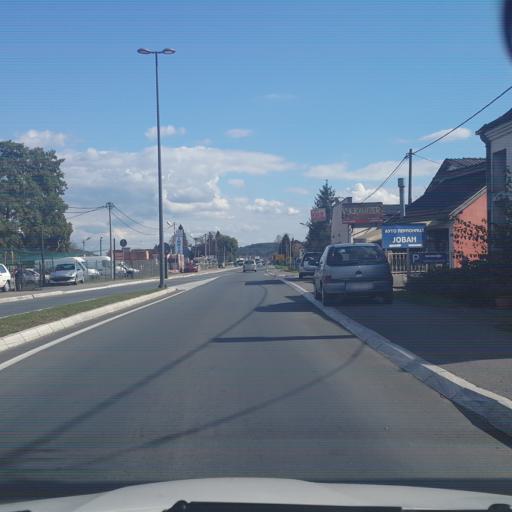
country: RS
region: Central Serbia
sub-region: Raski Okrug
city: Vrnjacka Banja
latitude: 43.6399
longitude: 20.9213
